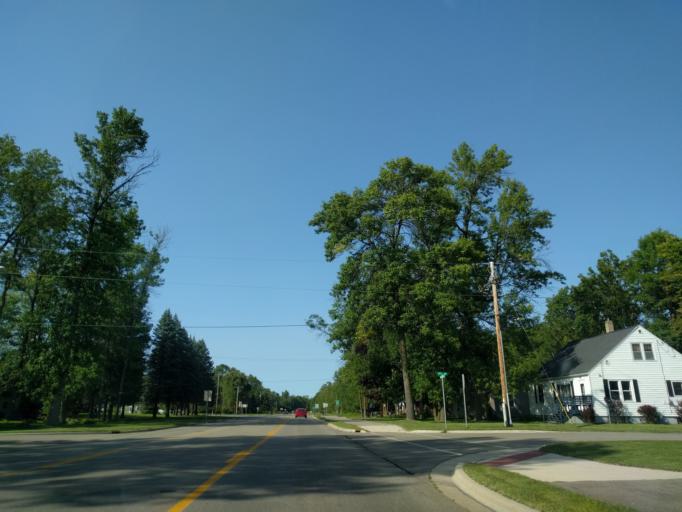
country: US
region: Michigan
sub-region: Menominee County
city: Menominee
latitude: 45.1428
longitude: -87.6032
